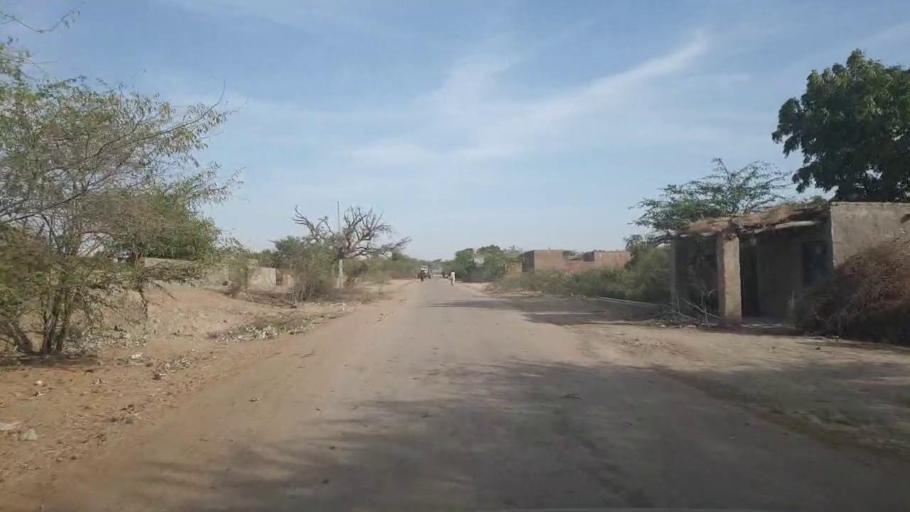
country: PK
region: Sindh
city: Nabisar
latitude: 25.0707
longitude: 69.6426
